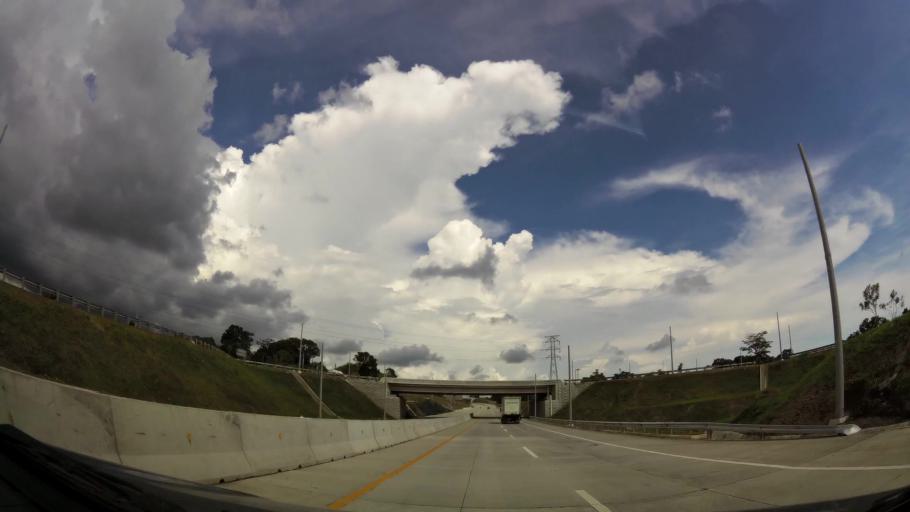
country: PA
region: Panama
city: Tocumen
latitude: 9.0910
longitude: -79.4317
